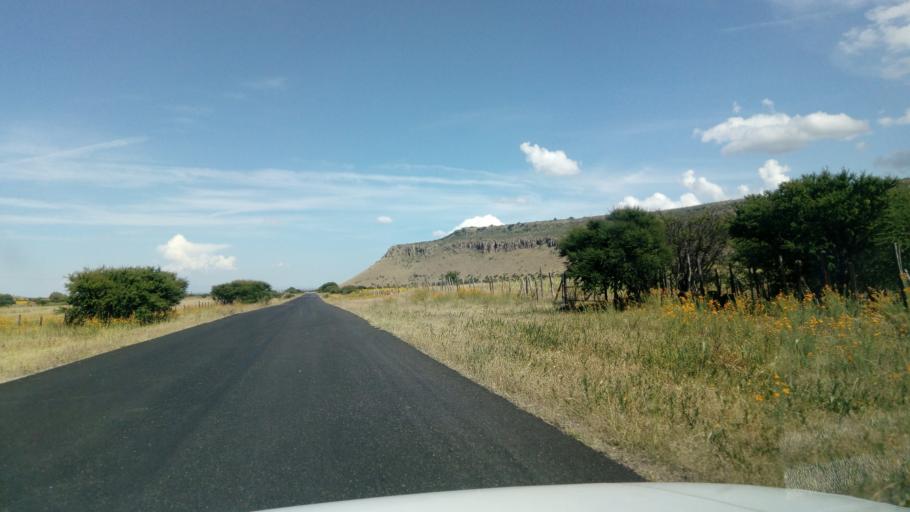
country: MX
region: Durango
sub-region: Durango
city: Jose Refugio Salcido
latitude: 23.8134
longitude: -104.4836
